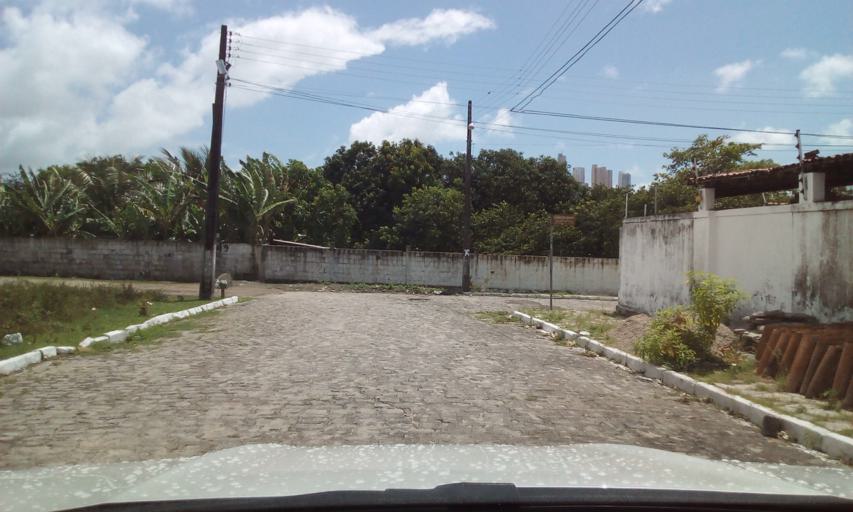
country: BR
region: Paraiba
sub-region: Joao Pessoa
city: Joao Pessoa
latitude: -7.1426
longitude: -34.8362
